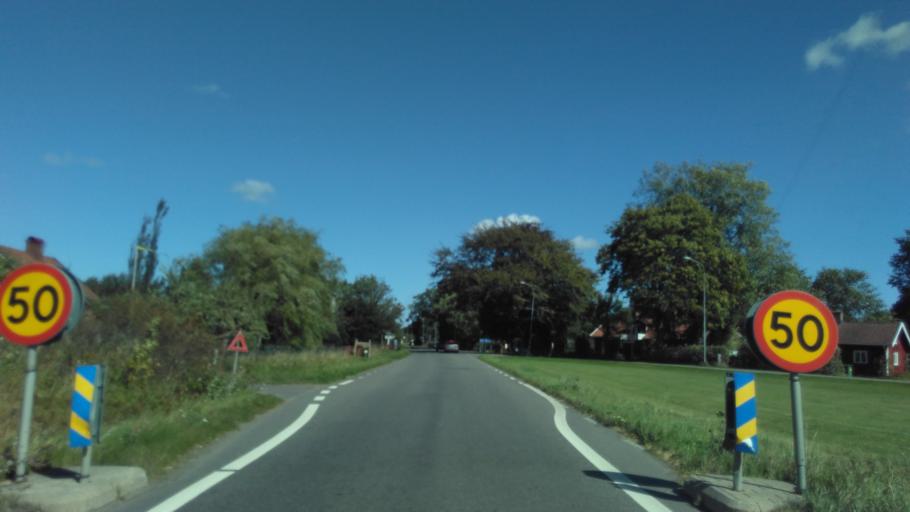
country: SE
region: Vaestra Goetaland
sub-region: Skara Kommun
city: Axvall
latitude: 58.4302
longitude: 13.6386
